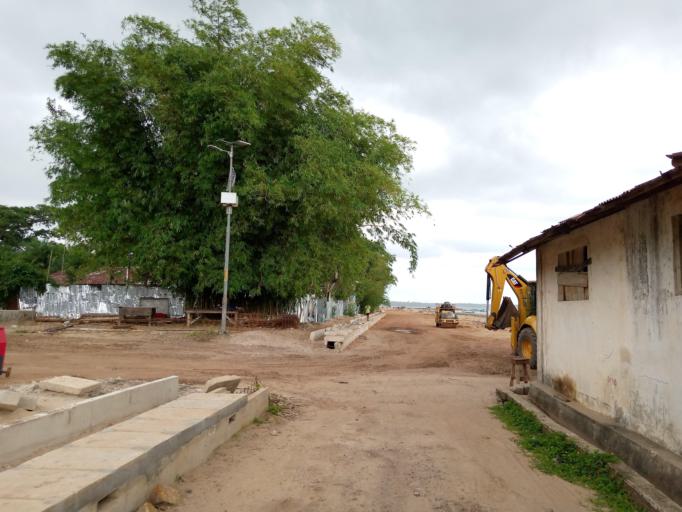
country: SL
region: Southern Province
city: Bonthe
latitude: 7.5267
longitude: -12.5003
